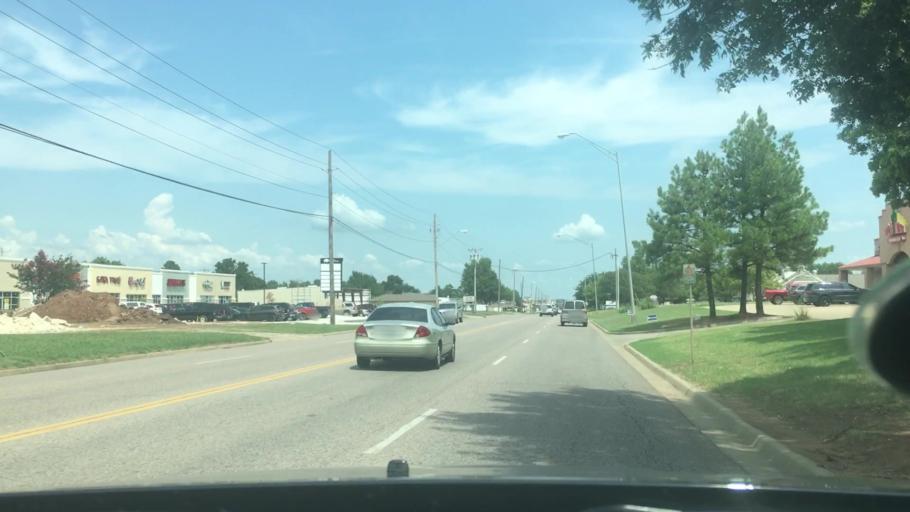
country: US
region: Oklahoma
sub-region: Pottawatomie County
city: Shawnee
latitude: 35.3698
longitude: -96.9297
